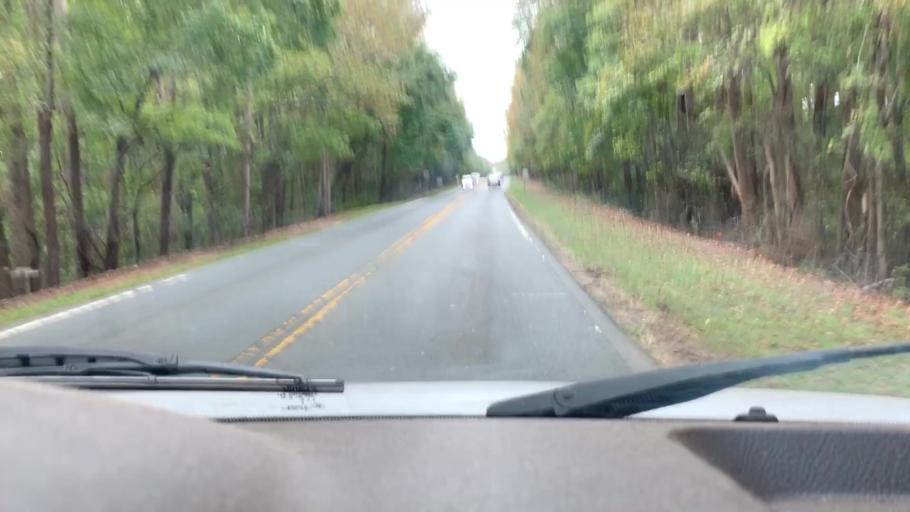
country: US
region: North Carolina
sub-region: Mecklenburg County
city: Cornelius
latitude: 35.4543
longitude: -80.8675
